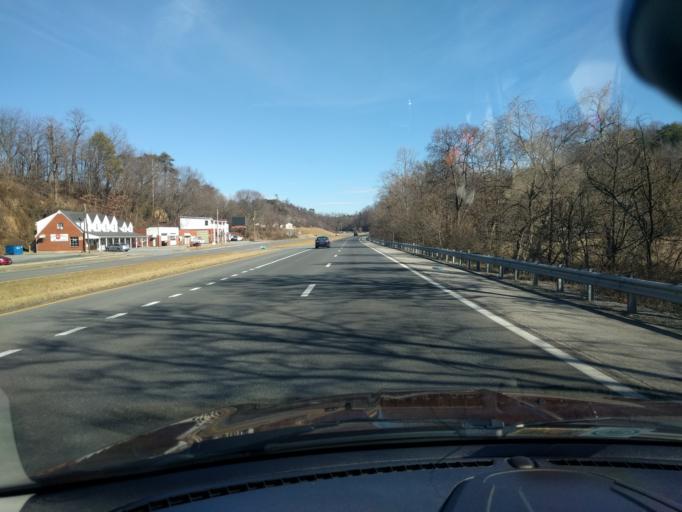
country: US
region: Virginia
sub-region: Botetourt County
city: Laymantown
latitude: 37.3364
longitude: -79.8575
